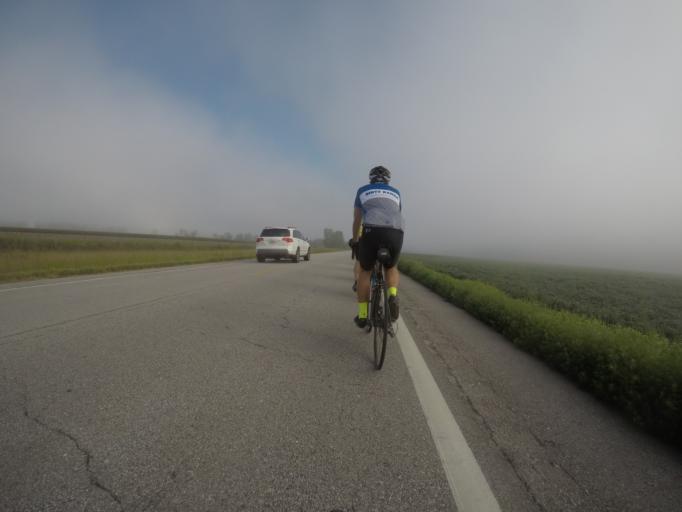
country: US
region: Missouri
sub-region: Platte County
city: Weston
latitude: 39.3581
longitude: -94.8688
